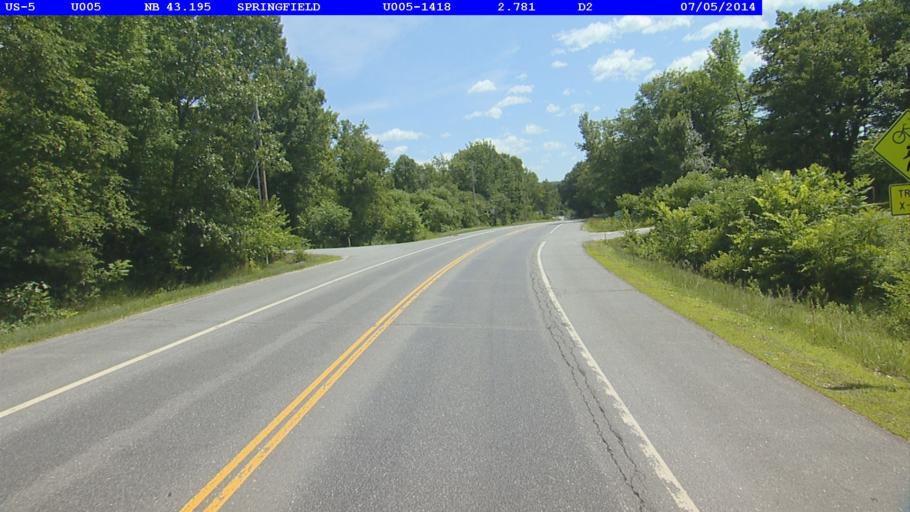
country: US
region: New Hampshire
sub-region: Sullivan County
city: Charlestown
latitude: 43.2650
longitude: -72.4288
